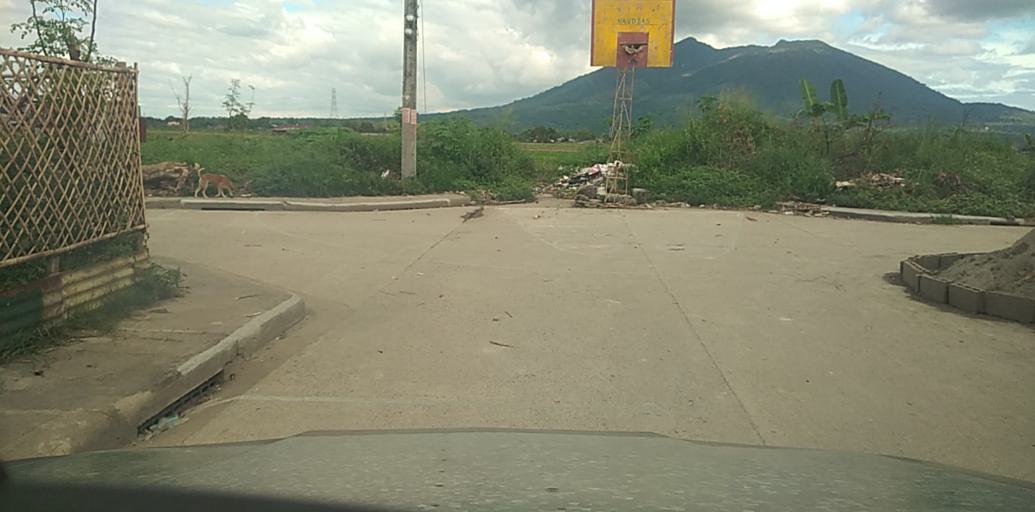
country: PH
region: Central Luzon
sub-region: Province of Pampanga
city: Buensuseso
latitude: 15.1821
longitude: 120.6673
